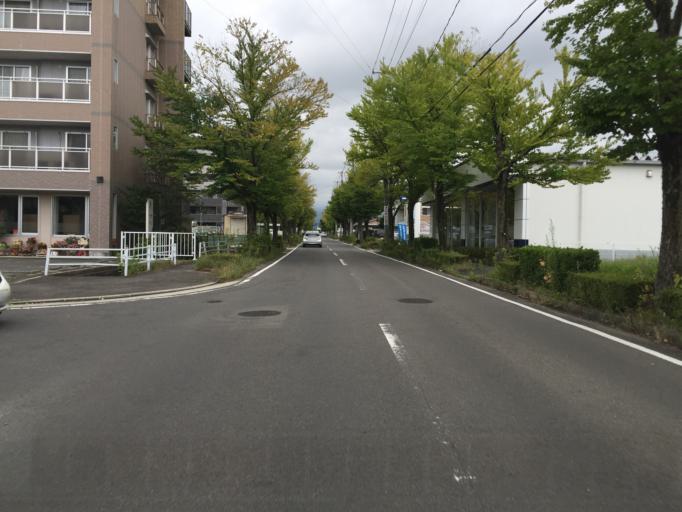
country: JP
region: Fukushima
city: Fukushima-shi
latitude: 37.7612
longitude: 140.4397
